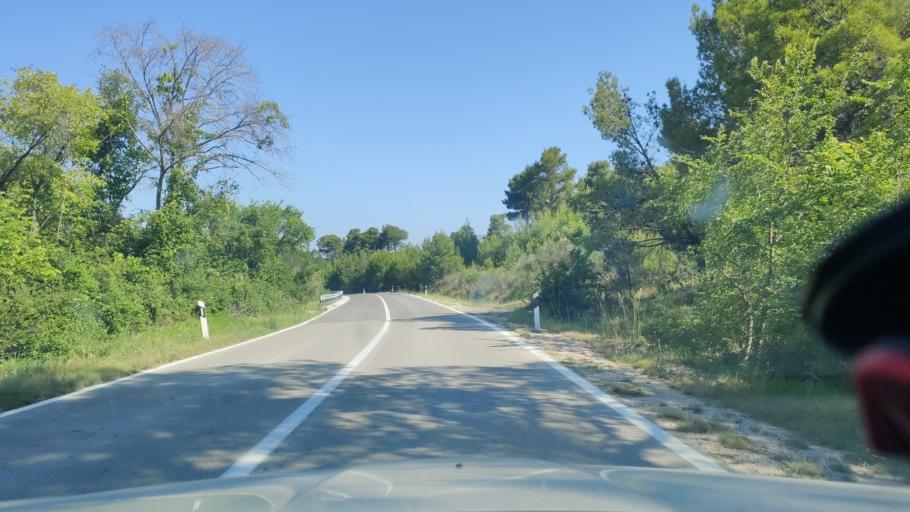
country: HR
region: Sibensko-Kniniska
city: Zaton
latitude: 43.9217
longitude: 15.8203
